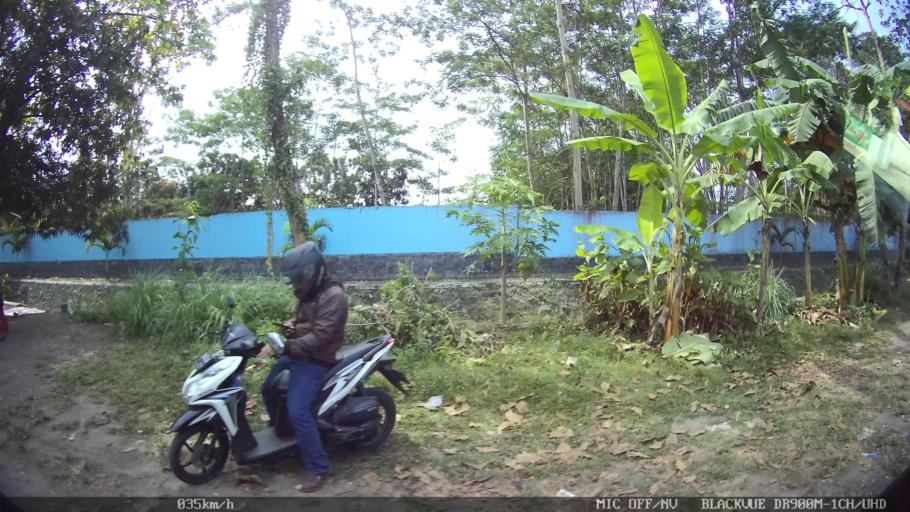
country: ID
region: Daerah Istimewa Yogyakarta
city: Depok
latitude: -7.8039
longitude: 110.4355
